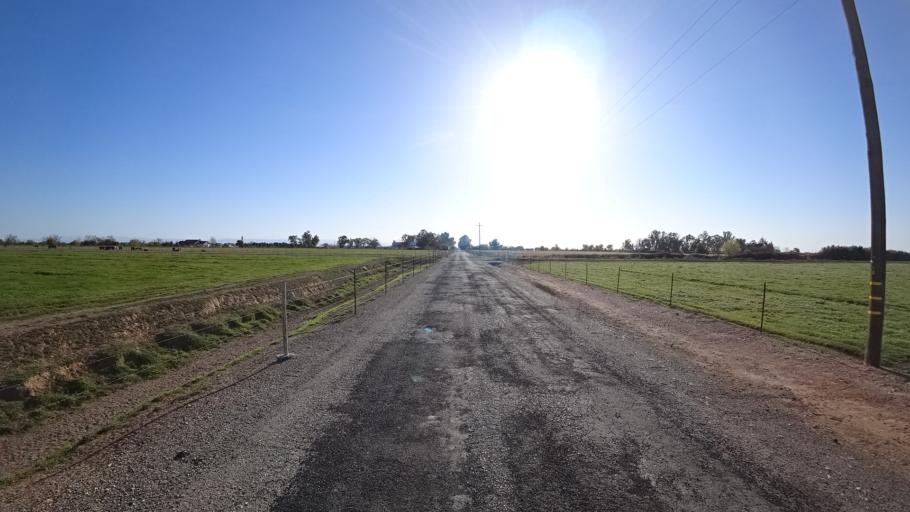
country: US
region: California
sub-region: Glenn County
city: Orland
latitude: 39.7589
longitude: -122.2532
